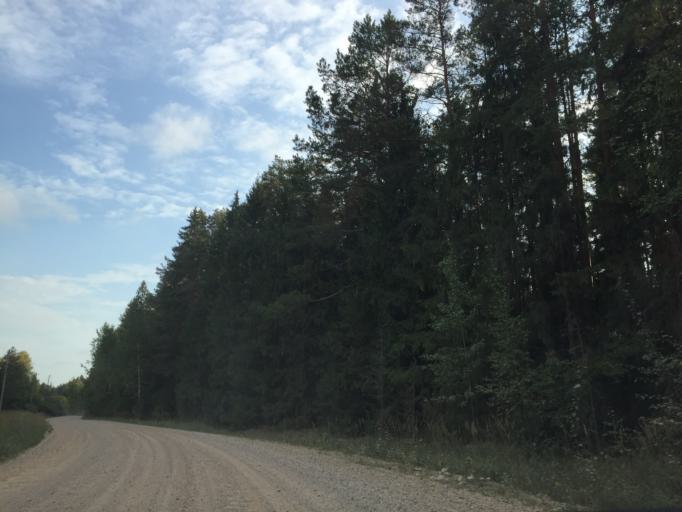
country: LV
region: Ikskile
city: Ikskile
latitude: 56.8000
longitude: 24.4370
